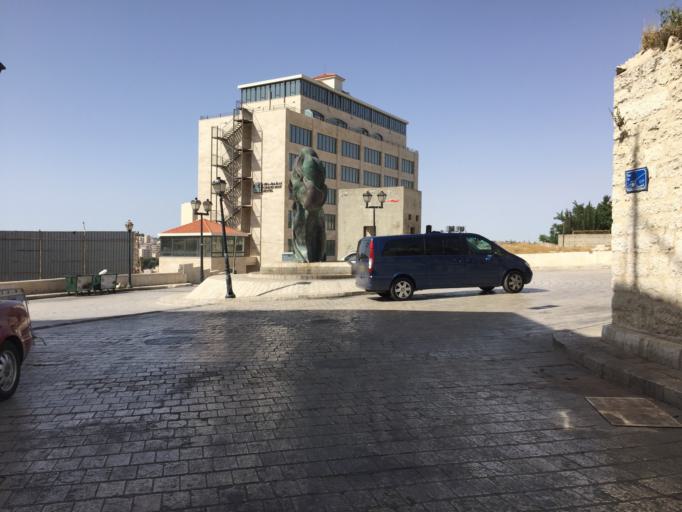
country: PS
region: West Bank
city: Bethlehem
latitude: 31.7090
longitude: 35.2044
